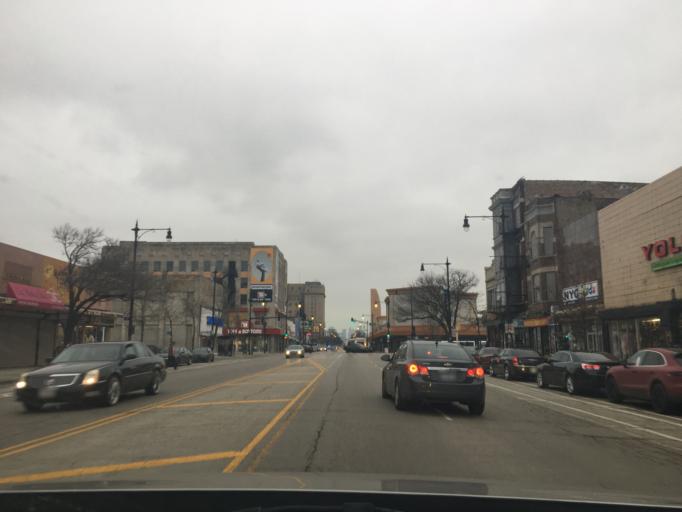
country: US
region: Illinois
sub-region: Cook County
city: Cicero
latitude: 41.8807
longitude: -87.7270
